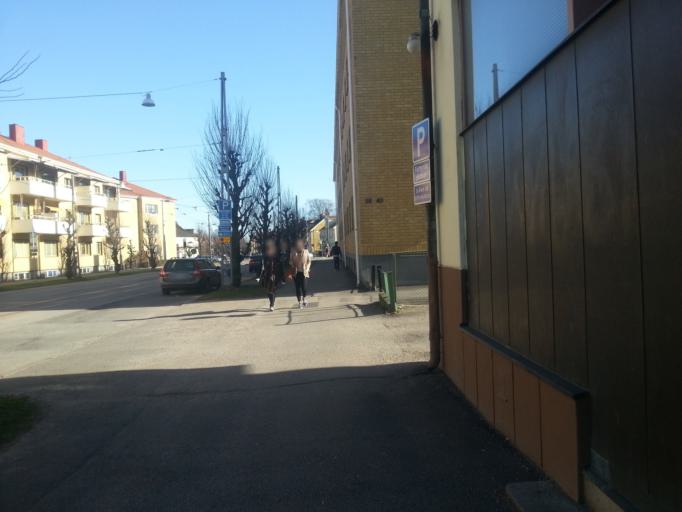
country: SE
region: OEstergoetland
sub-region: Norrkopings Kommun
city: Norrkoping
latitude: 58.5804
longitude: 16.1899
